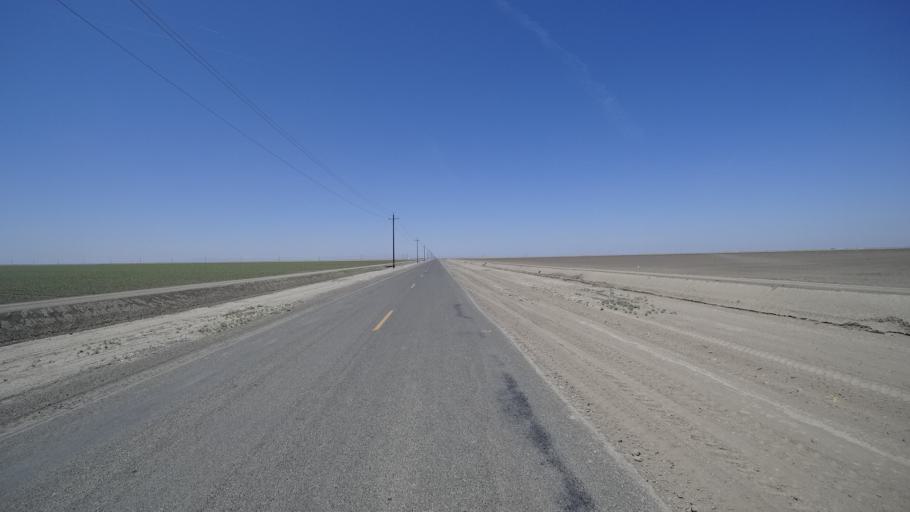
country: US
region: California
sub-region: Kings County
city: Corcoran
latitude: 36.0215
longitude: -119.6344
